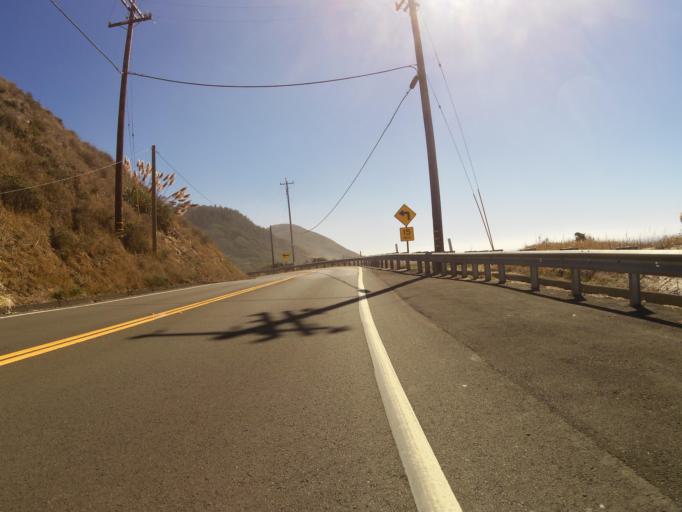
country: US
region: California
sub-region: Mendocino County
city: Fort Bragg
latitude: 39.6166
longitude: -123.7818
